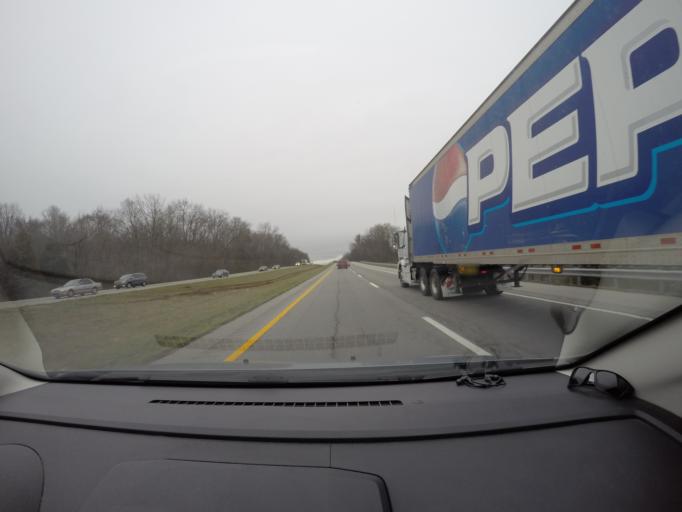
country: US
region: Tennessee
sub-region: Franklin County
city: Sewanee
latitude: 35.3391
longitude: -85.9395
